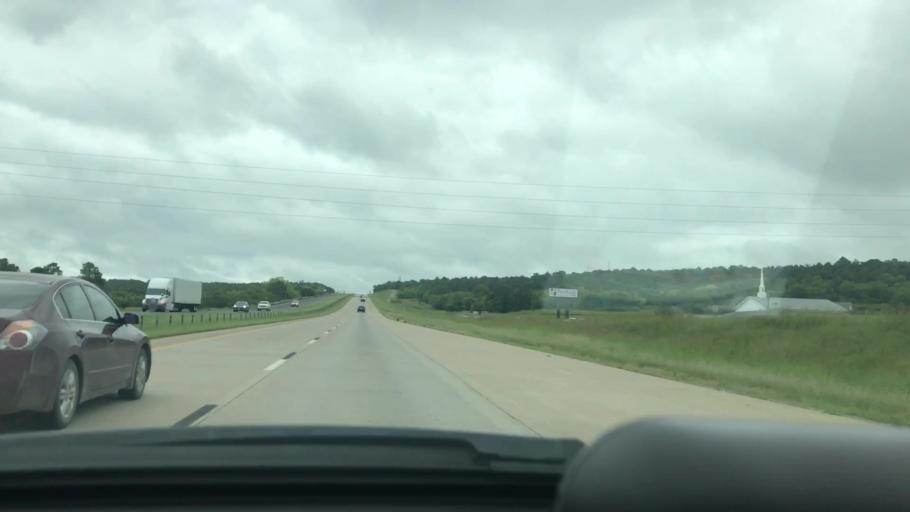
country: US
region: Oklahoma
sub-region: Pittsburg County
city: Krebs
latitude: 34.9596
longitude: -95.7248
